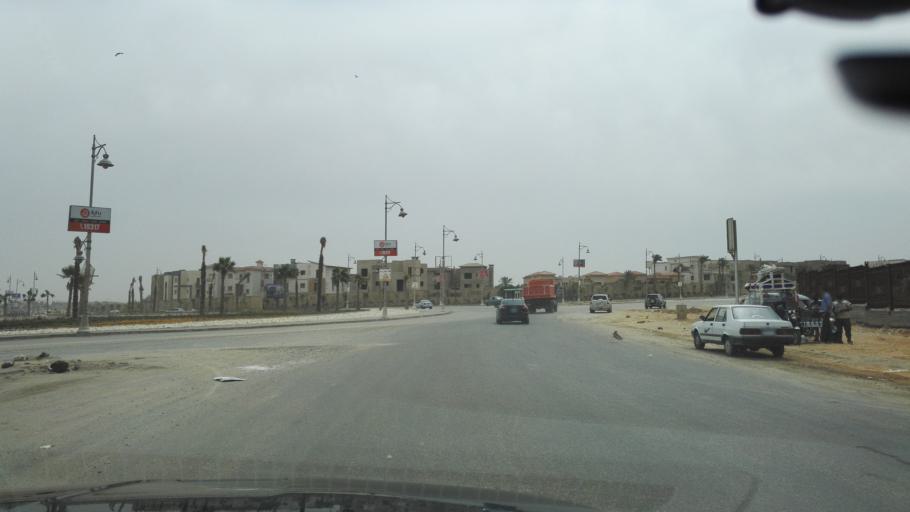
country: EG
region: Muhafazat al Qalyubiyah
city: Al Khankah
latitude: 30.0113
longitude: 31.5215
